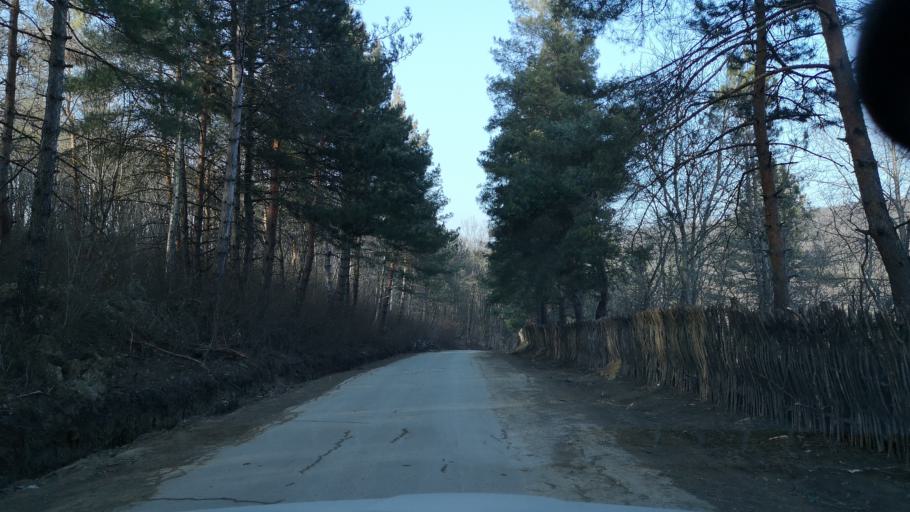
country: MD
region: Nisporeni
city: Nisporeni
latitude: 47.0812
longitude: 28.3222
